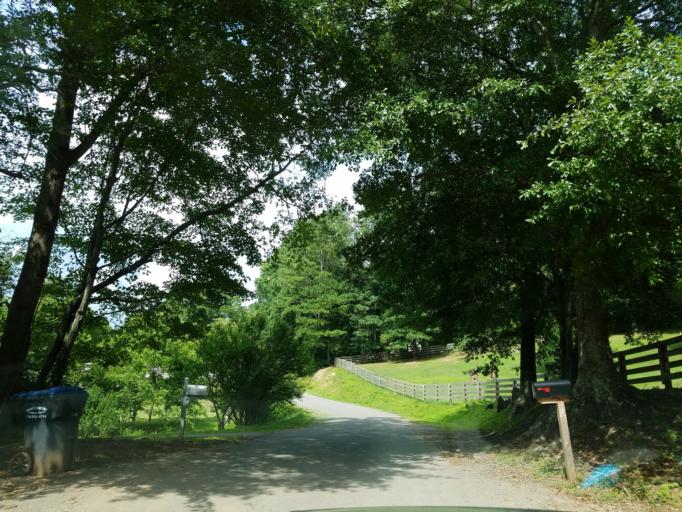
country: US
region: Georgia
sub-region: Cherokee County
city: Ball Ground
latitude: 34.3326
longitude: -84.3791
